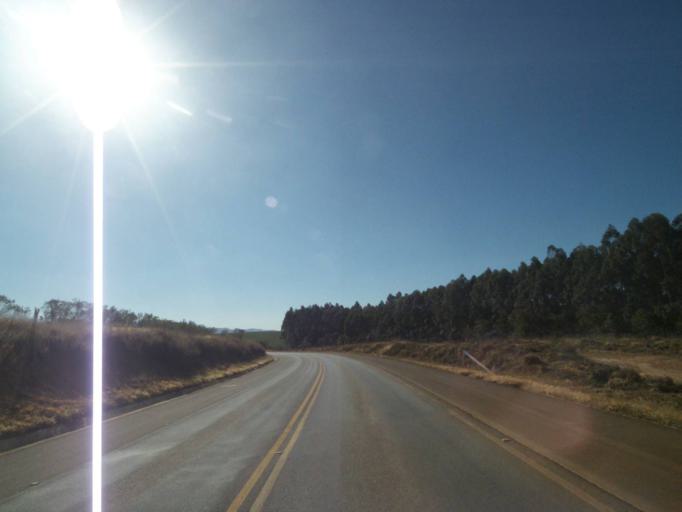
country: BR
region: Parana
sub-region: Tibagi
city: Tibagi
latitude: -24.6893
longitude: -50.4400
